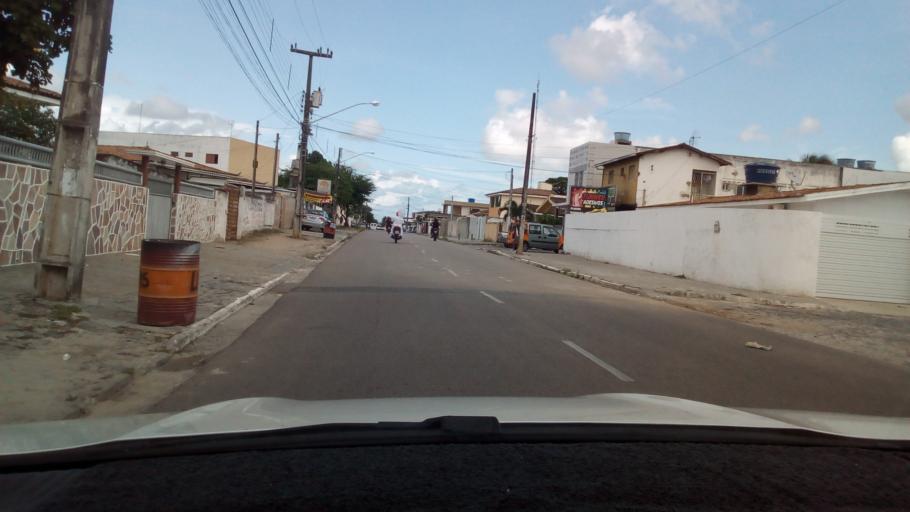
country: BR
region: Paraiba
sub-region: Joao Pessoa
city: Joao Pessoa
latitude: -7.1523
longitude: -34.8746
